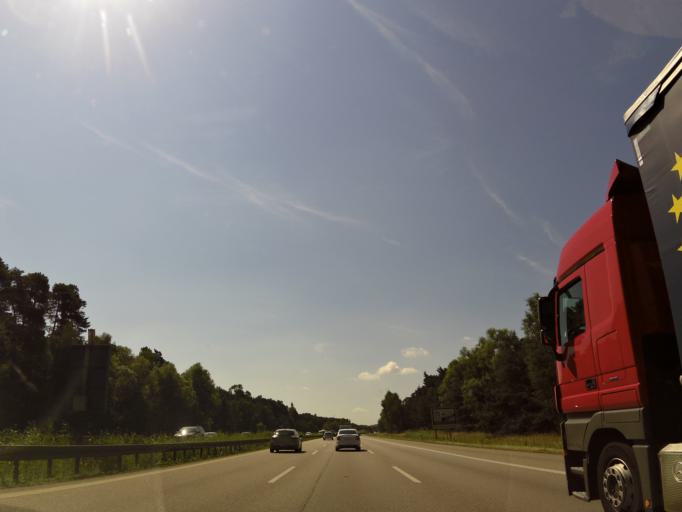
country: DE
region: Bavaria
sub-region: Upper Bavaria
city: Reichertshofen
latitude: 48.6686
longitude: 11.5085
